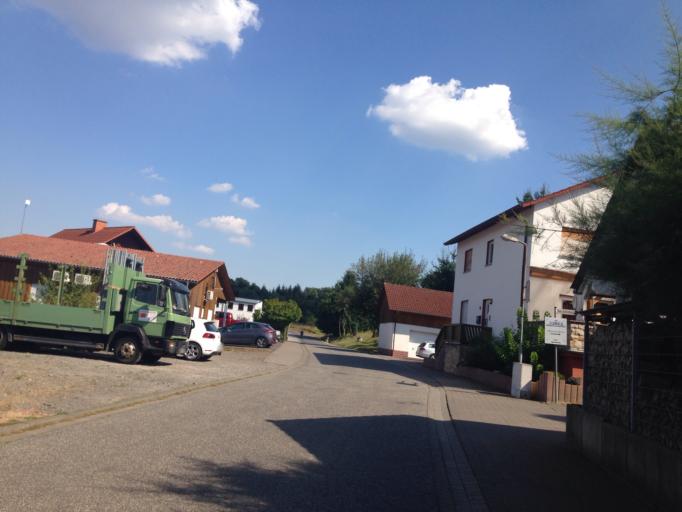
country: DE
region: Hesse
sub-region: Regierungsbezirk Giessen
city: Rabenau
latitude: 50.6735
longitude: 8.8267
